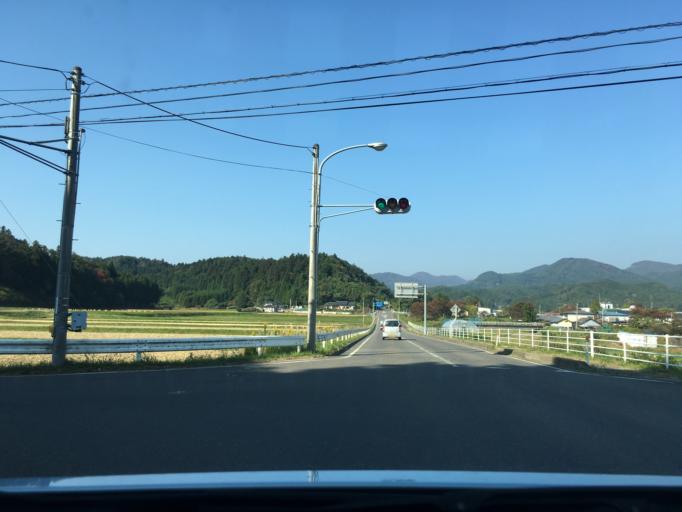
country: JP
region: Fukushima
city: Sukagawa
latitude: 37.2877
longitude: 140.2162
